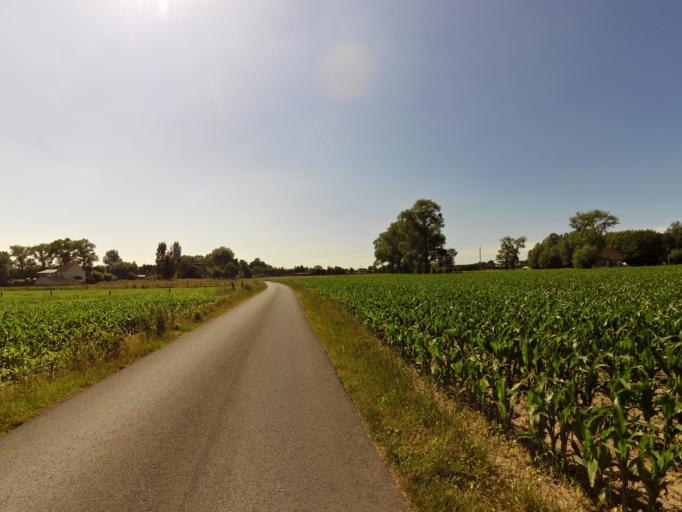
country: BE
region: Flanders
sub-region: Provincie West-Vlaanderen
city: Oudenburg
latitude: 51.1606
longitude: 3.0258
